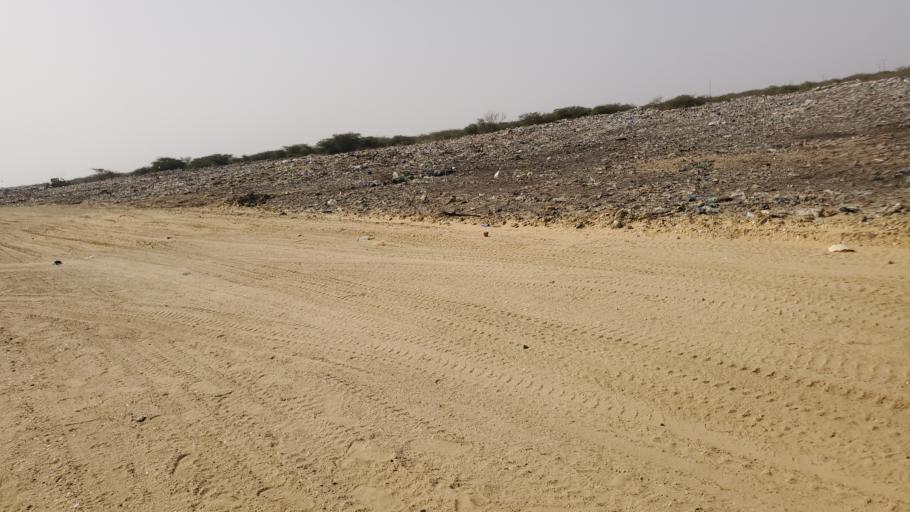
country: SN
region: Saint-Louis
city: Saint-Louis
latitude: 15.9490
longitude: -16.4329
